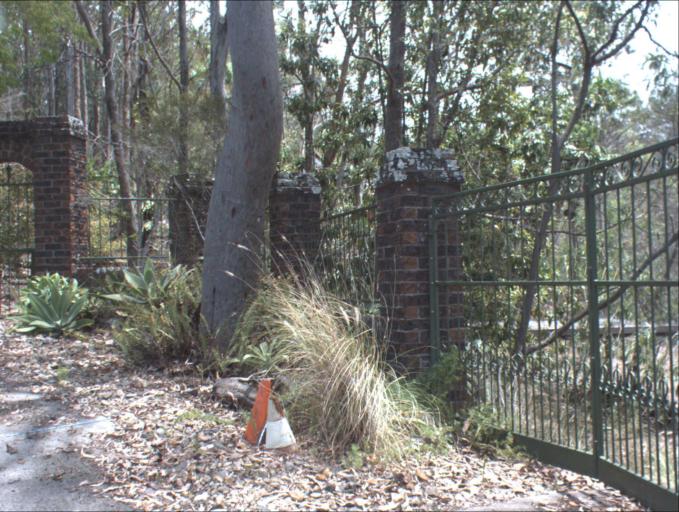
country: AU
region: Queensland
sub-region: Logan
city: Slacks Creek
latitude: -27.6609
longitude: 153.1973
